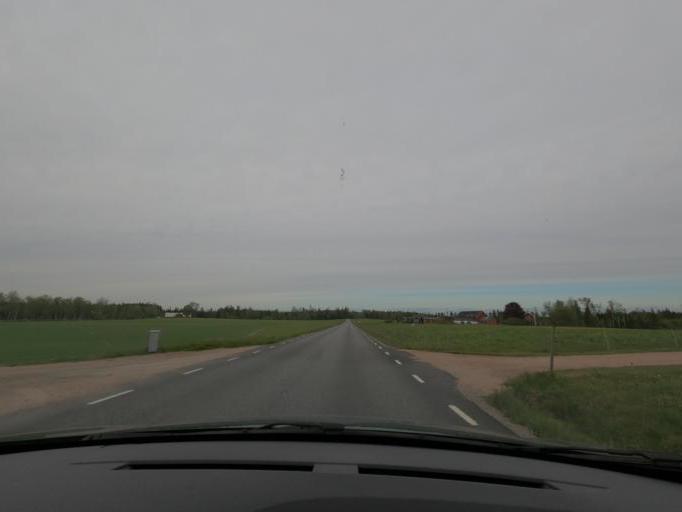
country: SE
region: Joenkoeping
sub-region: Varnamo Kommun
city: Bredaryd
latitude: 57.1455
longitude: 13.7208
